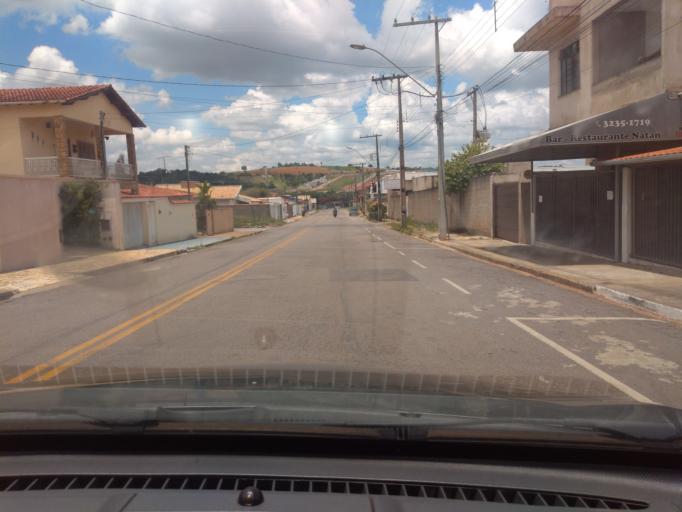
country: BR
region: Minas Gerais
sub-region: Tres Coracoes
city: Tres Coracoes
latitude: -21.6764
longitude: -45.2684
